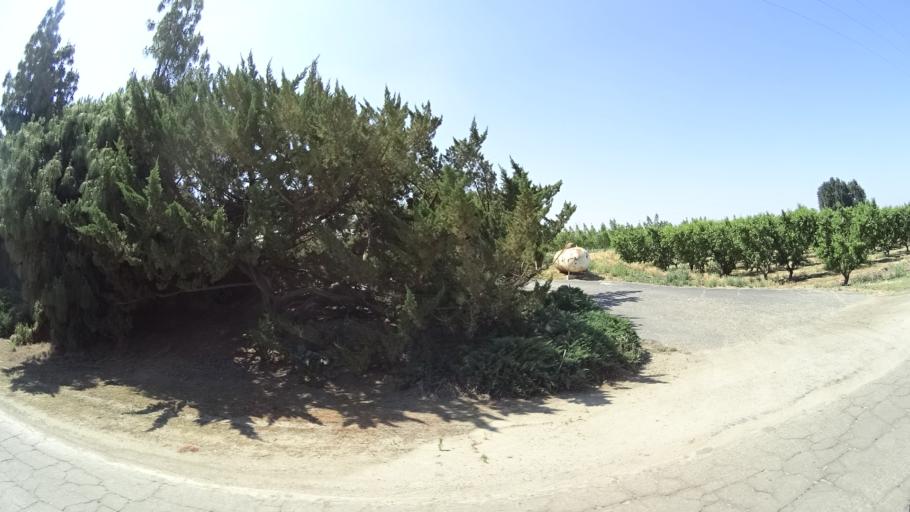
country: US
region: California
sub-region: Fresno County
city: Kingsburg
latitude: 36.4741
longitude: -119.5535
